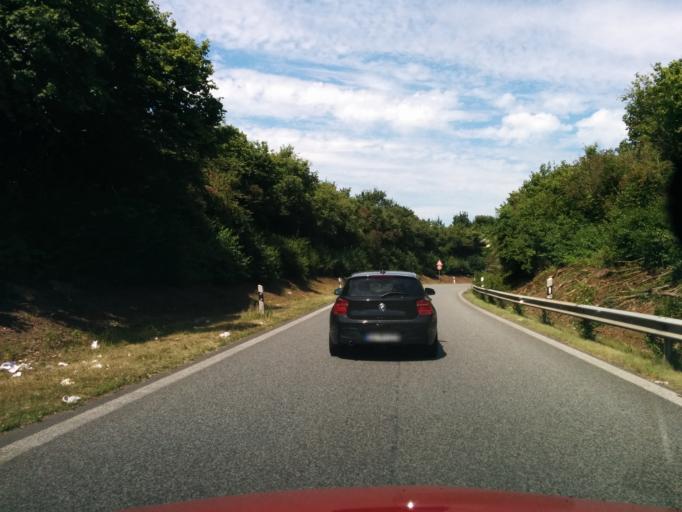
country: DE
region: Rheinland-Pfalz
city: Lahnstein
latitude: 50.3279
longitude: 7.6050
